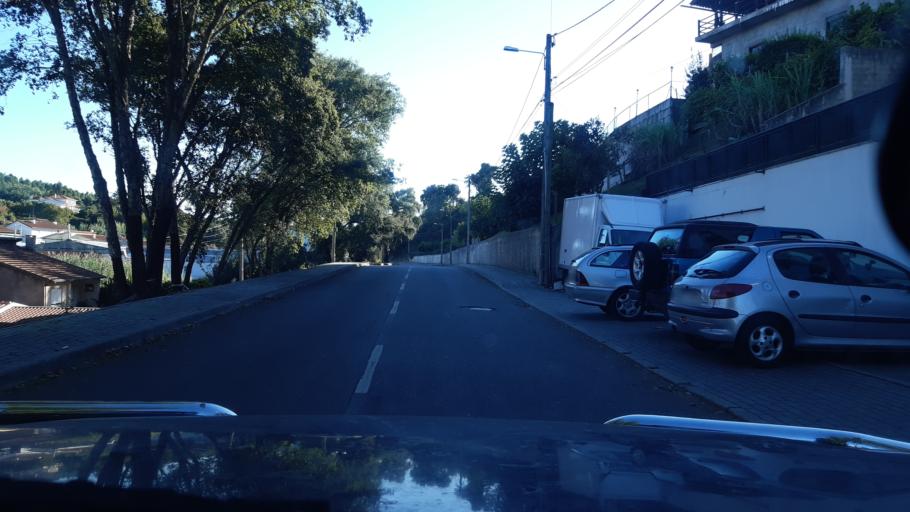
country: PT
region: Aveiro
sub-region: Agueda
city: Agueda
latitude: 40.5564
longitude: -8.4413
